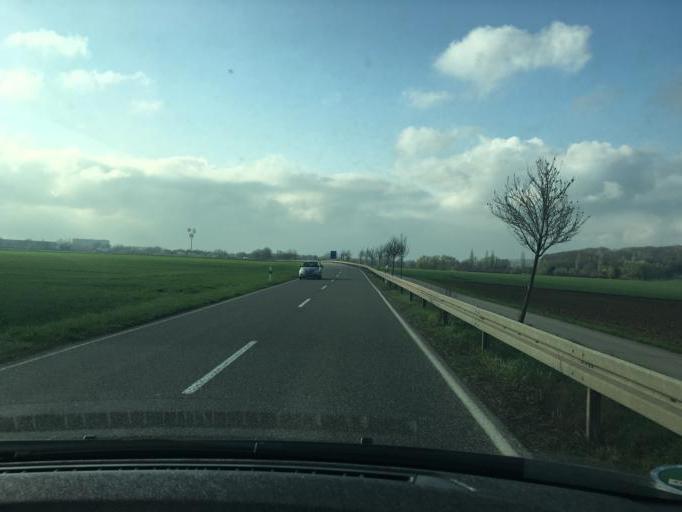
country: DE
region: North Rhine-Westphalia
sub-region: Regierungsbezirk Koln
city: Weilerswist
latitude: 50.7435
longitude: 6.8728
